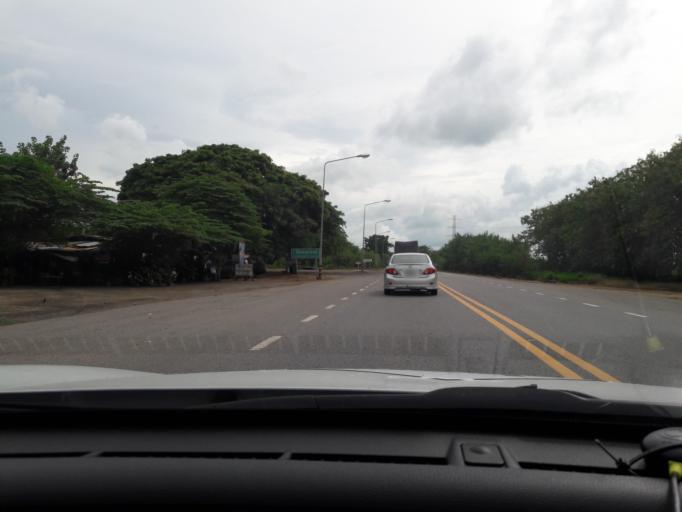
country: TH
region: Nakhon Sawan
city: Tak Fa
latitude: 15.4178
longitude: 100.5158
